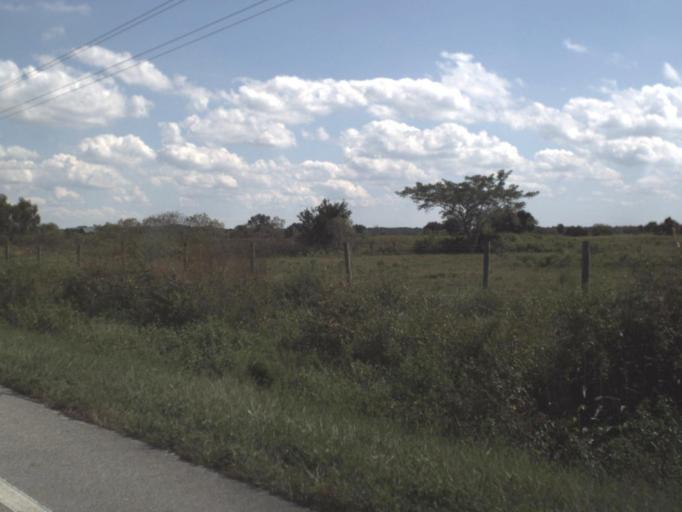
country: US
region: Florida
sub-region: Highlands County
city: Sebring
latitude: 27.4341
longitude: -81.3544
